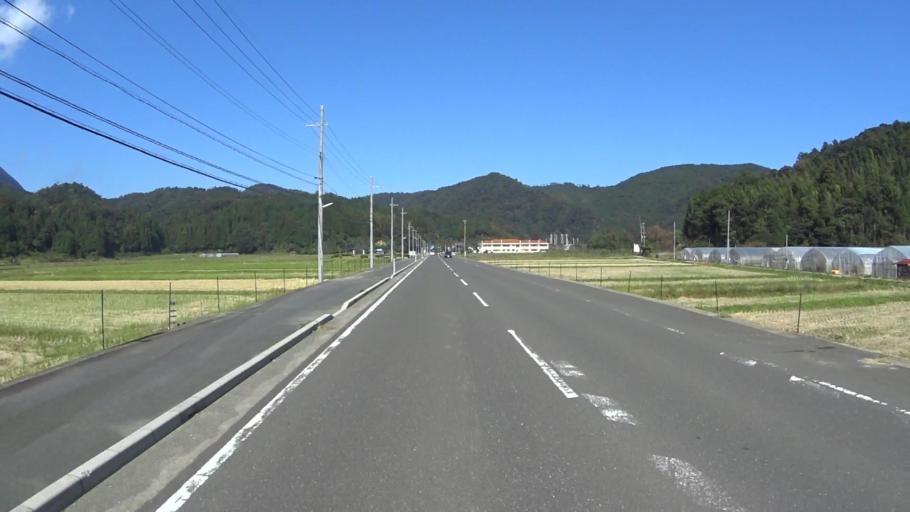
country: JP
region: Kyoto
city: Miyazu
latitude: 35.7234
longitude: 135.2547
